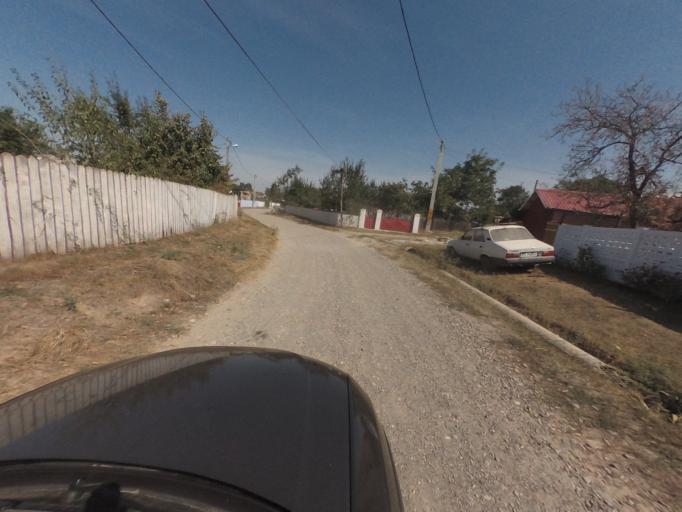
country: RO
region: Vaslui
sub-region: Comuna Deleni
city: Deleni
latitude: 46.5272
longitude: 27.7530
